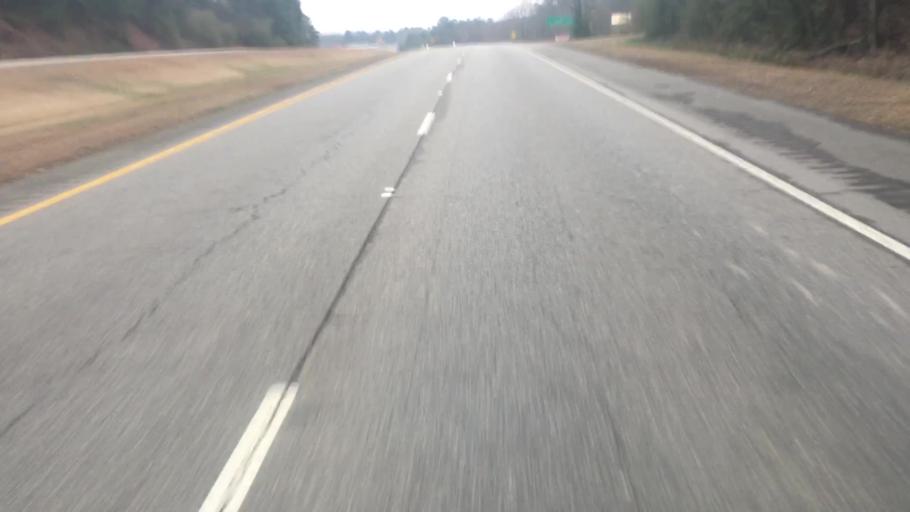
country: US
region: Alabama
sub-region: Walker County
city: Sumiton
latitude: 33.7655
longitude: -87.0699
